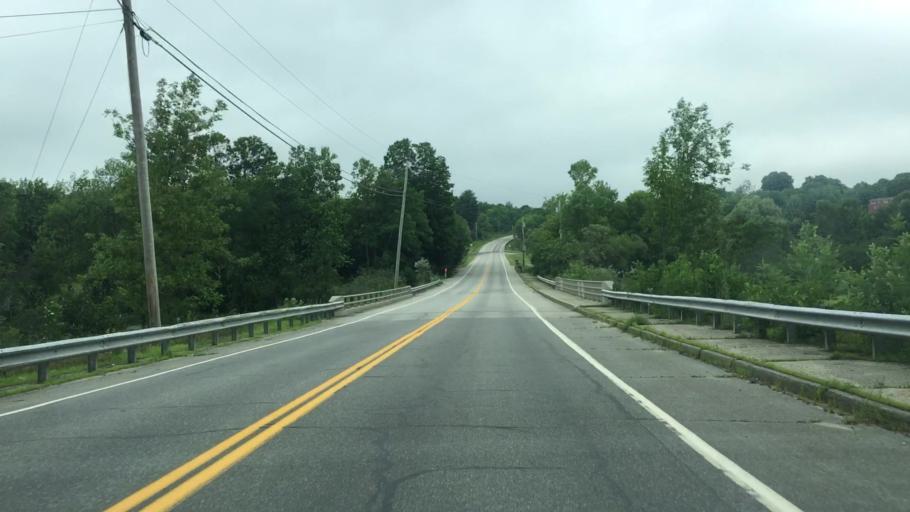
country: US
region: Maine
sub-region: Sagadahoc County
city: Richmond
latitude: 44.1085
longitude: -69.7261
